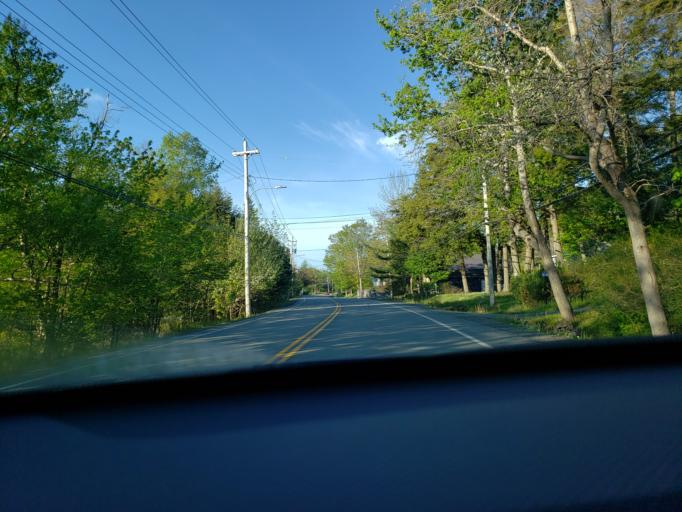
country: CA
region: Nova Scotia
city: Cole Harbour
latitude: 44.7384
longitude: -63.3875
